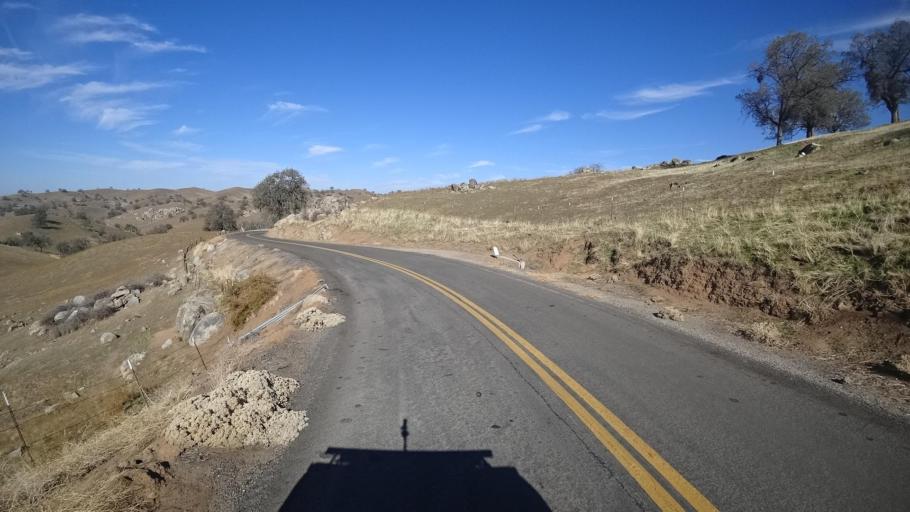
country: US
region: California
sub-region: Tulare County
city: Richgrove
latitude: 35.6973
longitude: -118.8588
